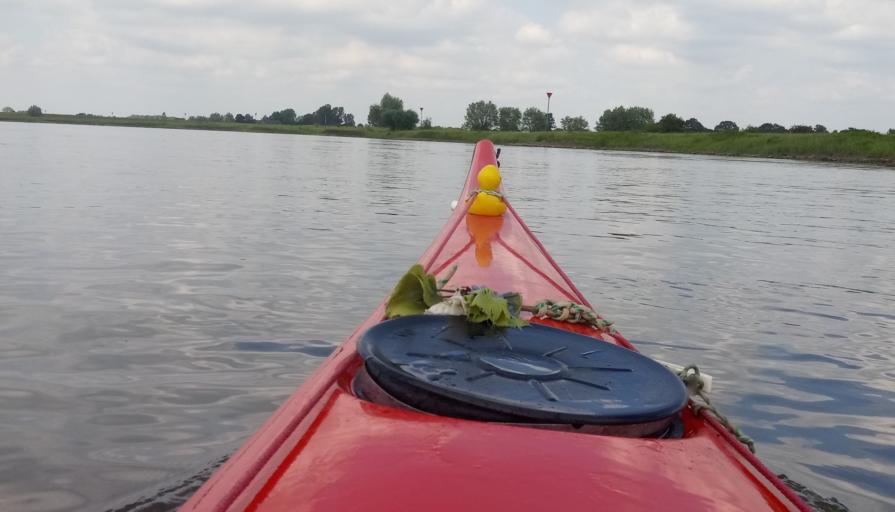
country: NL
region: Gelderland
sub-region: Gemeente Lochem
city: Gorssel
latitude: 52.1748
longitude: 6.1943
